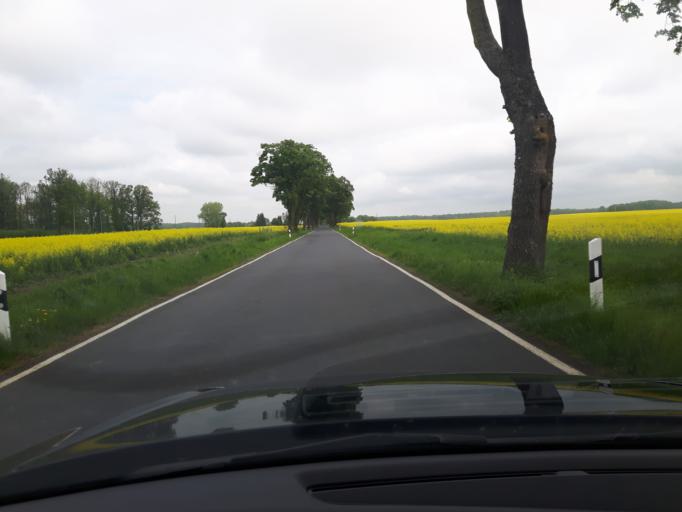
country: DE
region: Mecklenburg-Vorpommern
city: Velgast
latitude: 54.2068
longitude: 12.7318
